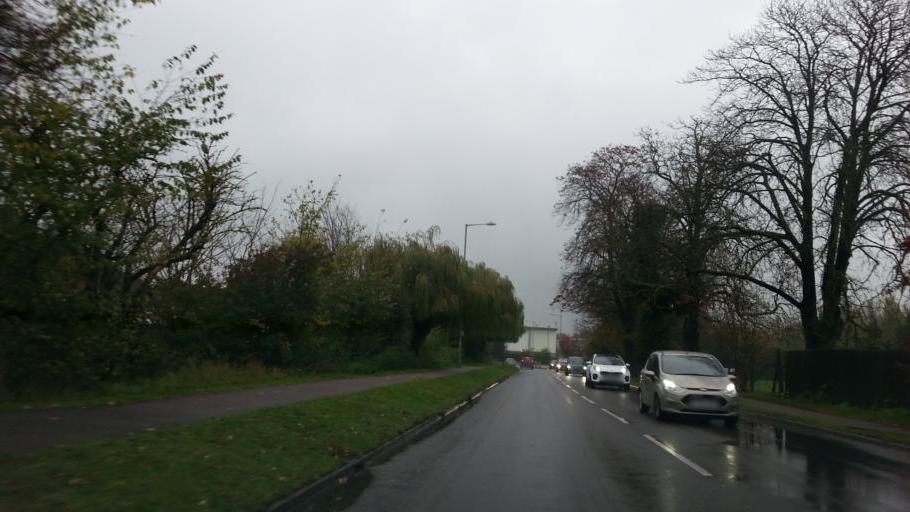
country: GB
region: England
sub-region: Suffolk
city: Haverhill
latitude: 52.0795
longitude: 0.4460
